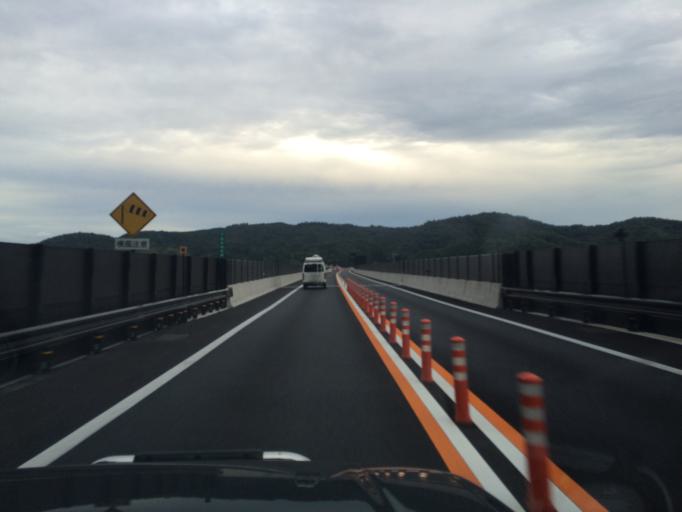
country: JP
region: Tottori
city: Tottori
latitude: 35.5002
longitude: 134.0640
